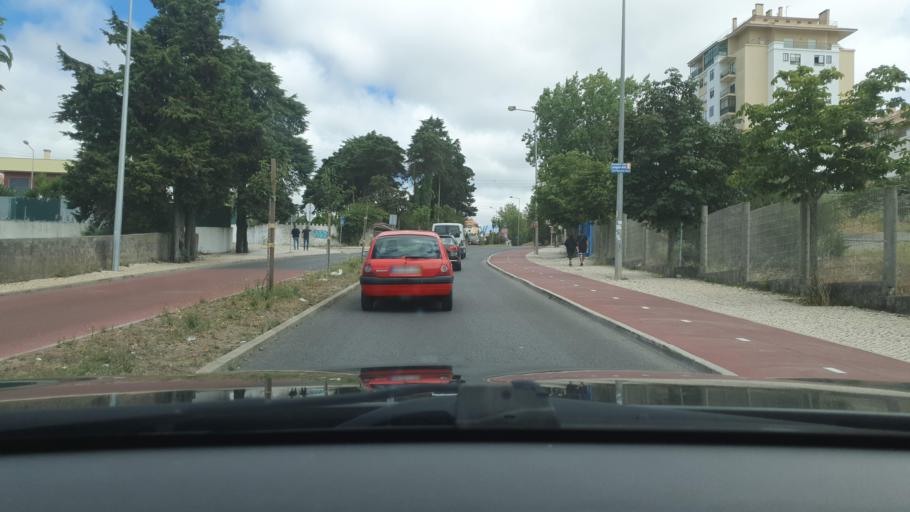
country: PT
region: Lisbon
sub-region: Sintra
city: Cacem
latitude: 38.7594
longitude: -9.2784
